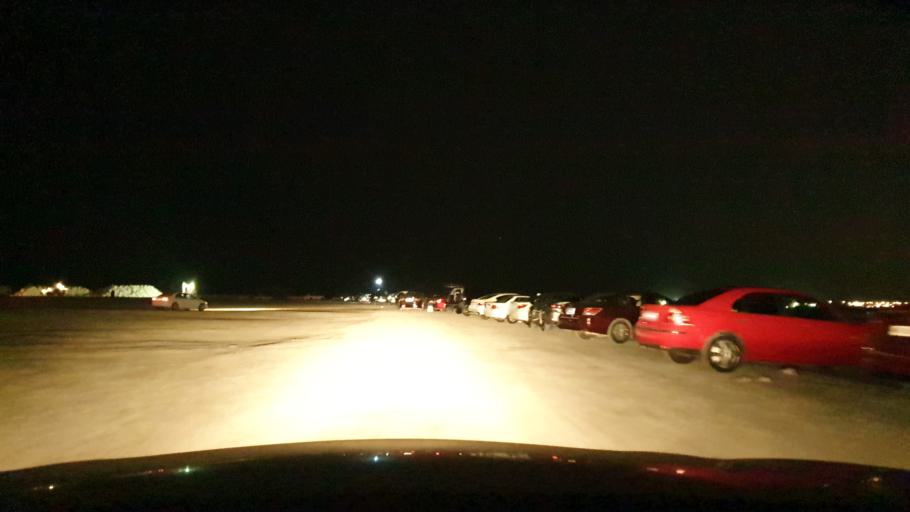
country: BH
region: Muharraq
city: Al Muharraq
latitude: 26.2551
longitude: 50.5840
